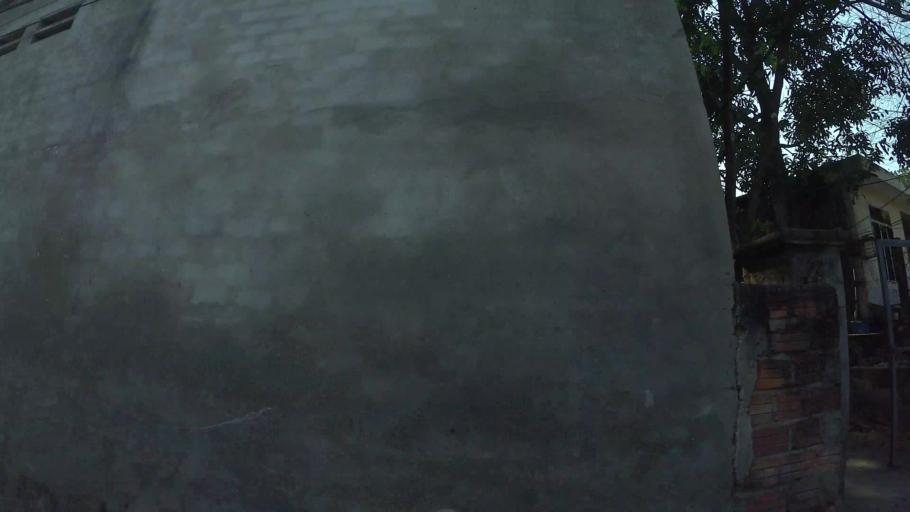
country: VN
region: Da Nang
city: Cam Le
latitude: 16.0121
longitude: 108.1855
